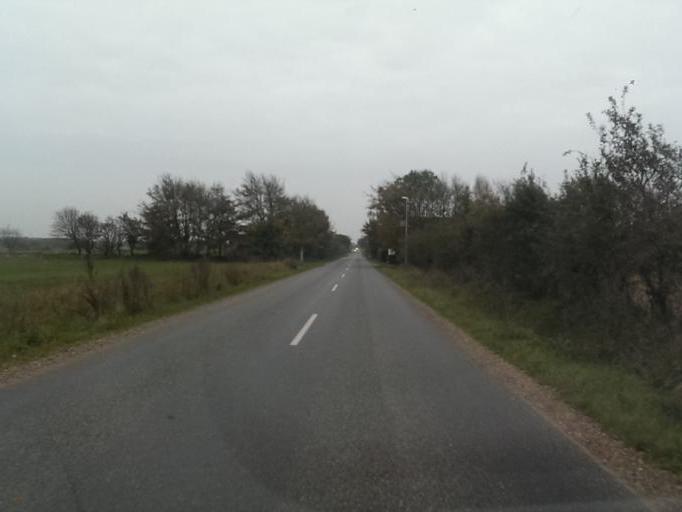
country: DK
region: South Denmark
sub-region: Esbjerg Kommune
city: Tjaereborg
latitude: 55.4823
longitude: 8.5555
